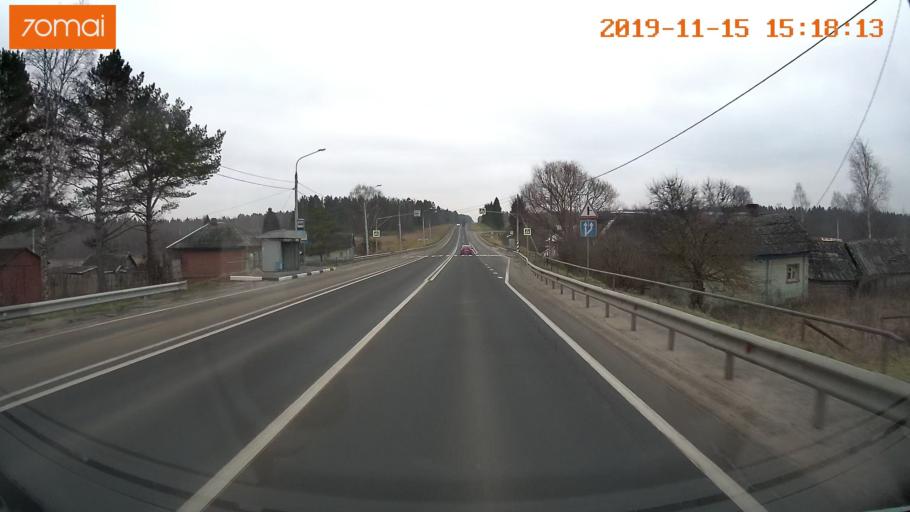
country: RU
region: Jaroslavl
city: Danilov
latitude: 58.2505
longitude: 40.1807
